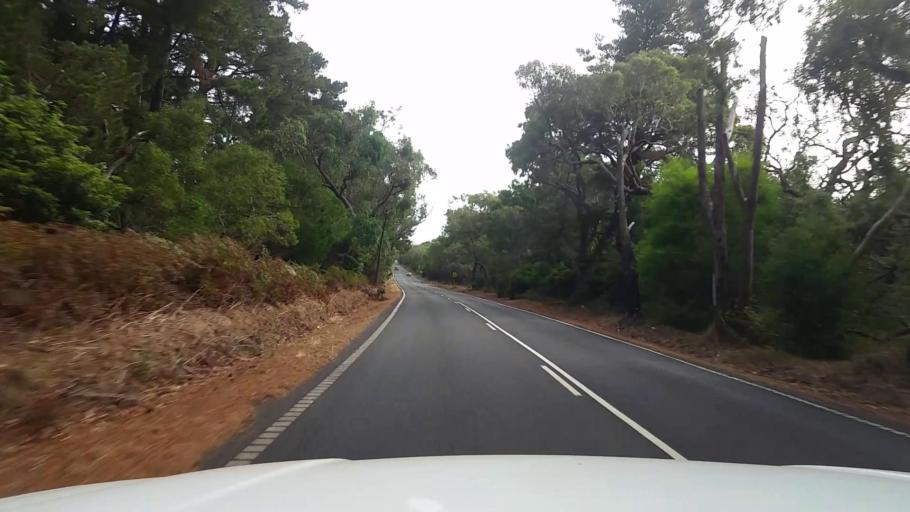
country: AU
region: Victoria
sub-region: Mornington Peninsula
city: Balnarring
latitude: -38.3256
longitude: 145.0925
